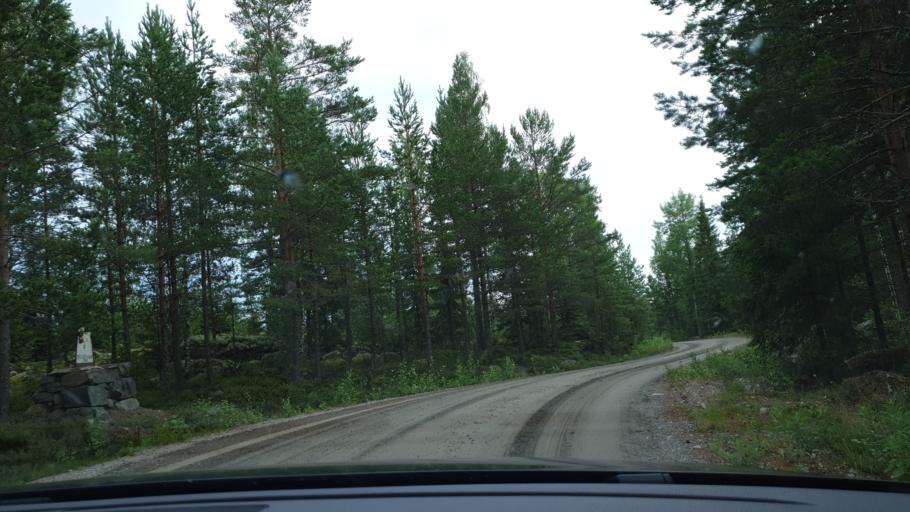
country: SE
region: Gaevleborg
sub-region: Hudiksvalls Kommun
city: Iggesund
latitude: 61.5229
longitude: 17.0160
